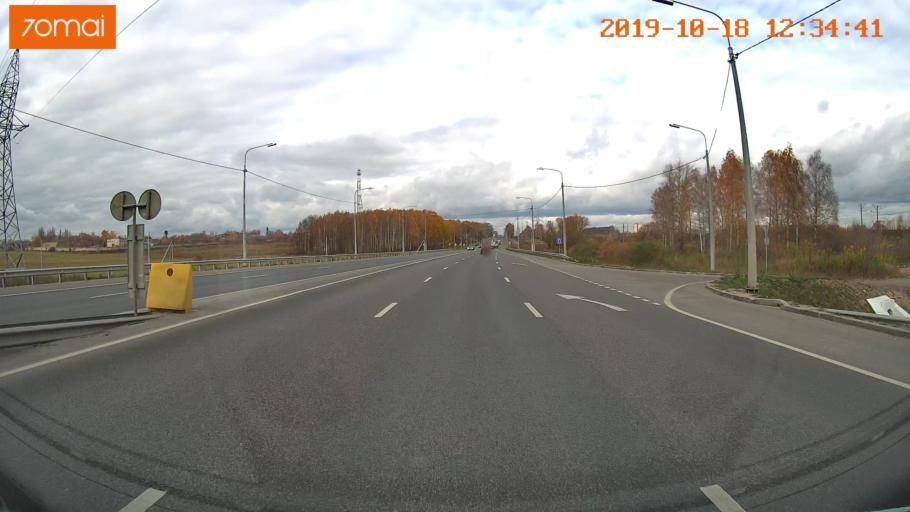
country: RU
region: Rjazan
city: Ryazan'
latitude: 54.6166
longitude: 39.6371
